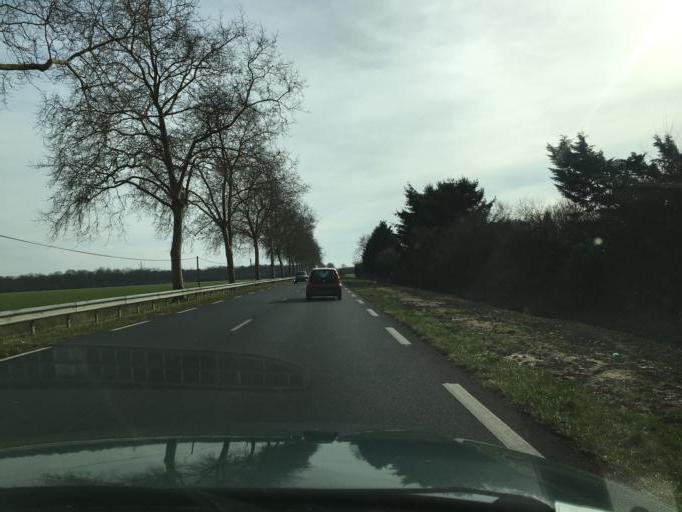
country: FR
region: Centre
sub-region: Departement du Loiret
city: Saint-Cyr-en-Val
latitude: 47.8038
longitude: 1.9304
